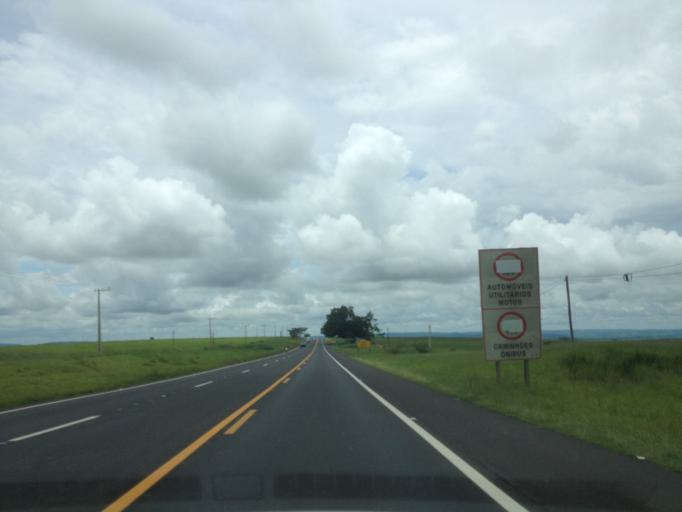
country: BR
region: Sao Paulo
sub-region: Marilia
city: Marilia
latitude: -22.2610
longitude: -49.9937
